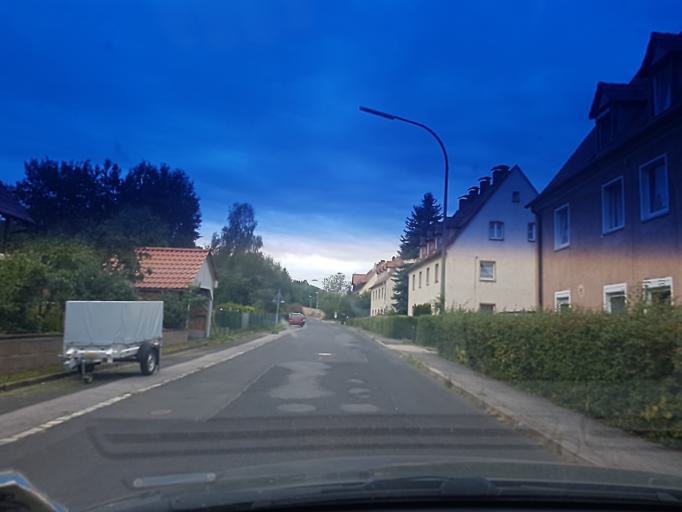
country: DE
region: Bavaria
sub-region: Upper Franconia
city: Burgwindheim
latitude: 49.8400
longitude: 10.5173
